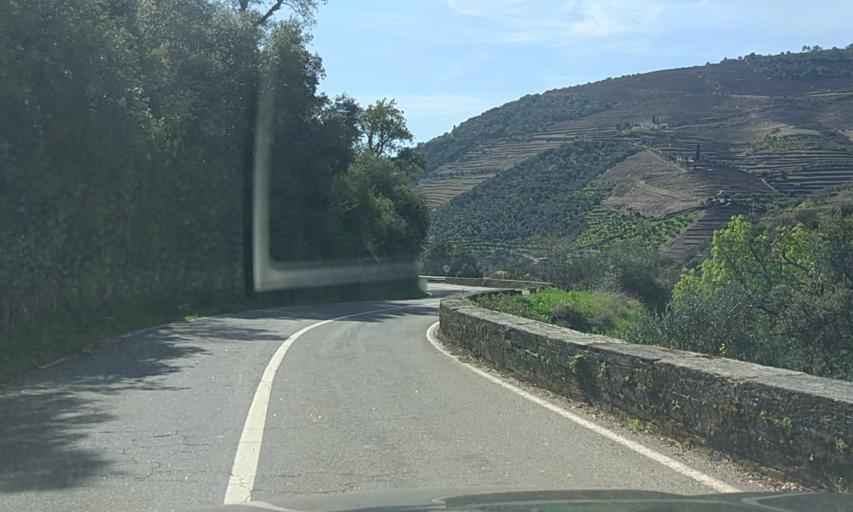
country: PT
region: Vila Real
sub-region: Sabrosa
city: Vilela
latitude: 41.2001
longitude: -7.5426
